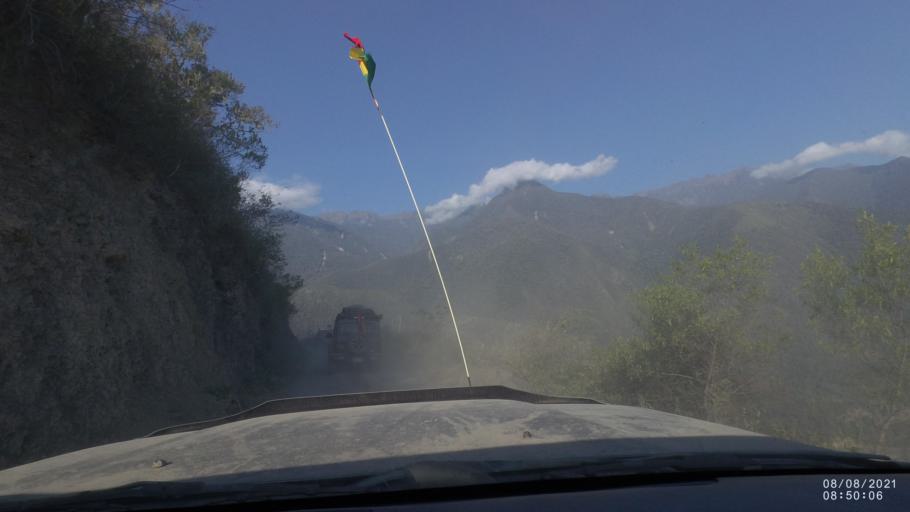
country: BO
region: La Paz
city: Quime
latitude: -16.5339
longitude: -66.7592
